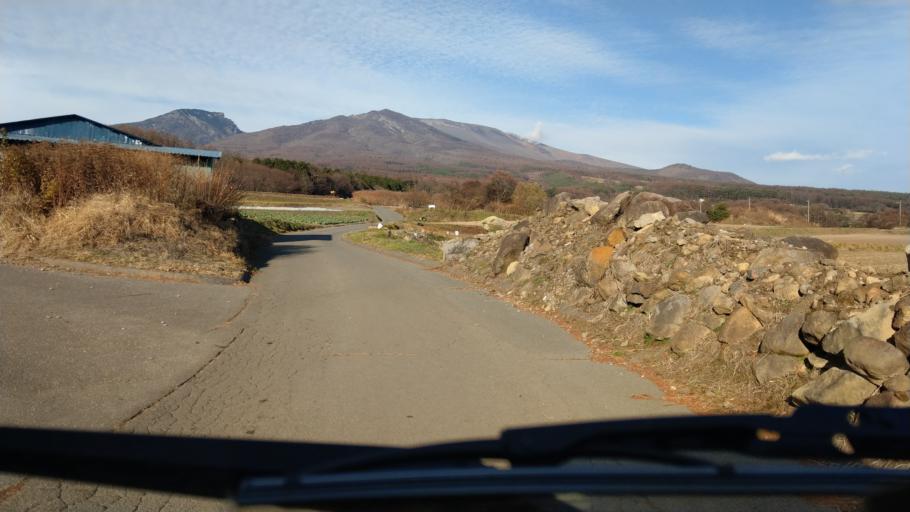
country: JP
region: Nagano
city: Komoro
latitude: 36.3402
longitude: 138.4760
